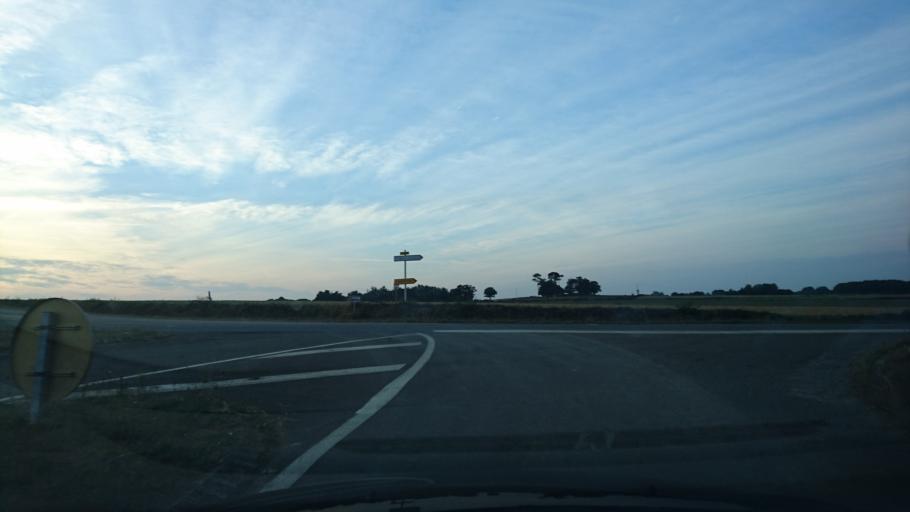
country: FR
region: Brittany
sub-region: Departement d'Ille-et-Vilaine
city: Maure-de-Bretagne
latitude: 47.8668
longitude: -2.0595
